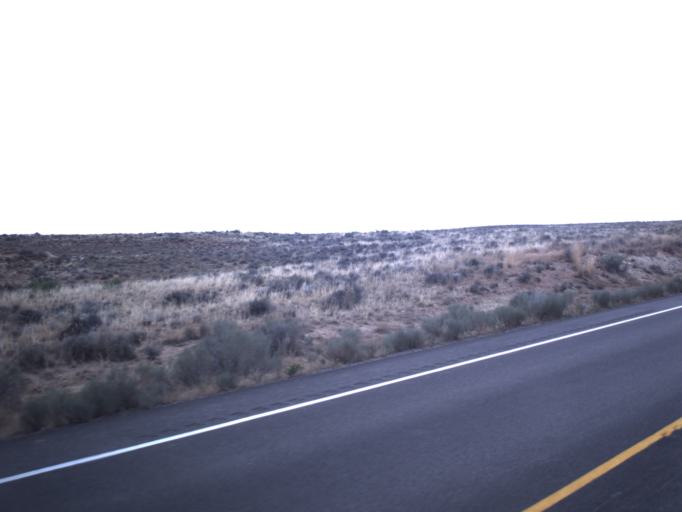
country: US
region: Utah
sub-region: Uintah County
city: Naples
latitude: 40.2908
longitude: -109.4754
